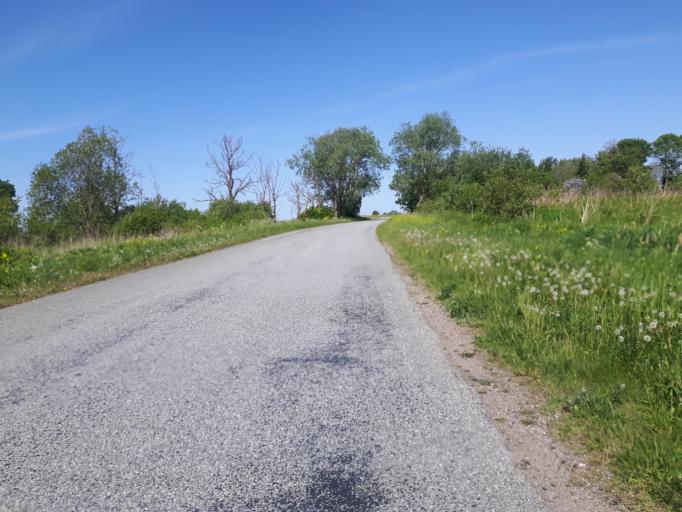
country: EE
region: Ida-Virumaa
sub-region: Aseri vald
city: Aseri
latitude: 59.4648
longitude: 26.8235
